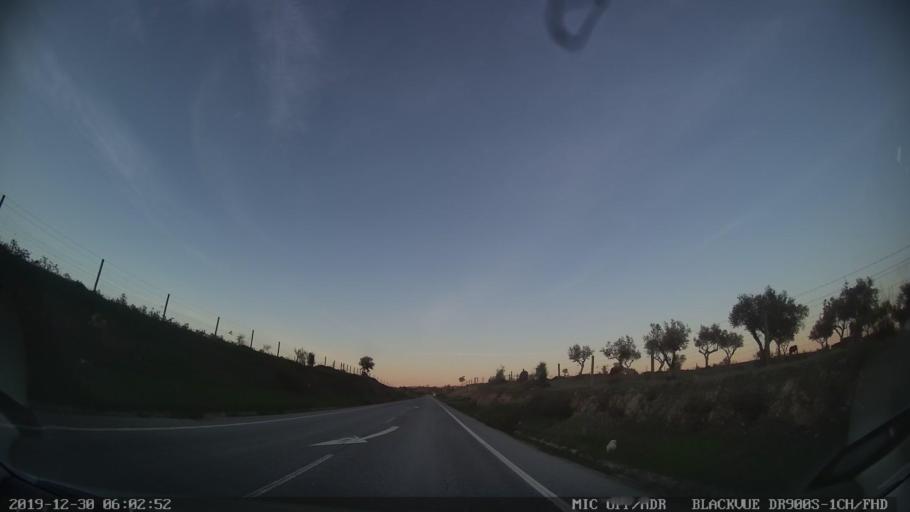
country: PT
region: Castelo Branco
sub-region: Penamacor
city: Penamacor
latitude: 40.0735
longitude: -7.2415
